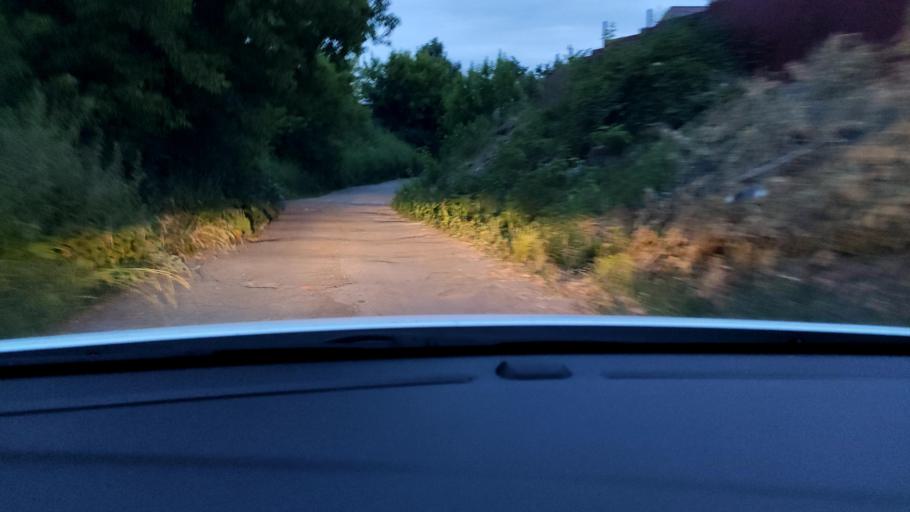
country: RU
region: Tatarstan
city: Stolbishchi
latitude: 55.7430
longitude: 49.2681
